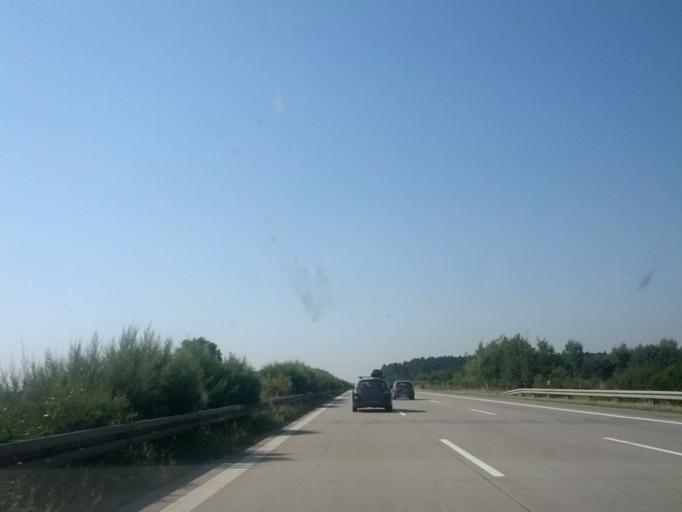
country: DE
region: Brandenburg
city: Linthe
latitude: 52.1494
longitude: 12.7714
